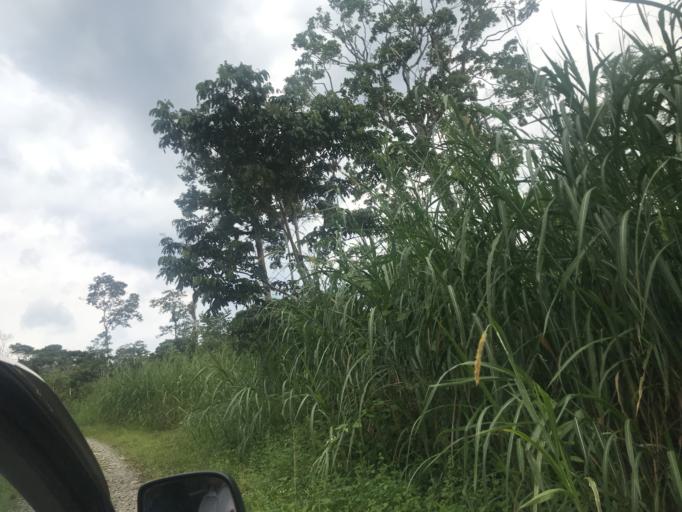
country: EC
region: Napo
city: Tena
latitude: -1.0208
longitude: -77.7420
